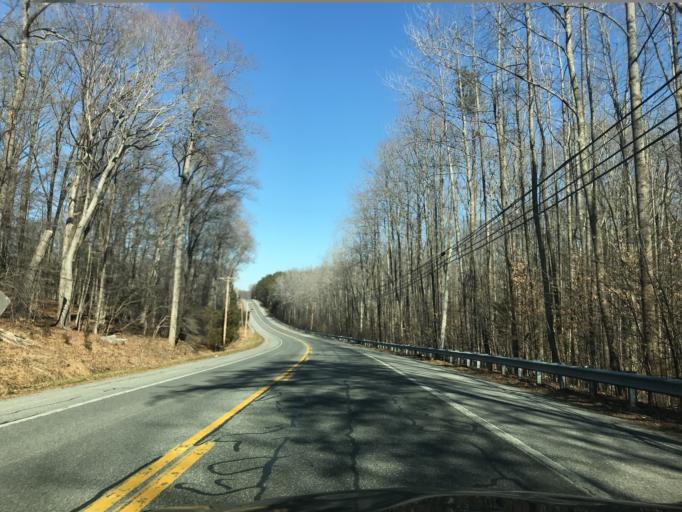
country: US
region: Maryland
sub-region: Charles County
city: Indian Head
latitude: 38.5463
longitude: -77.1770
